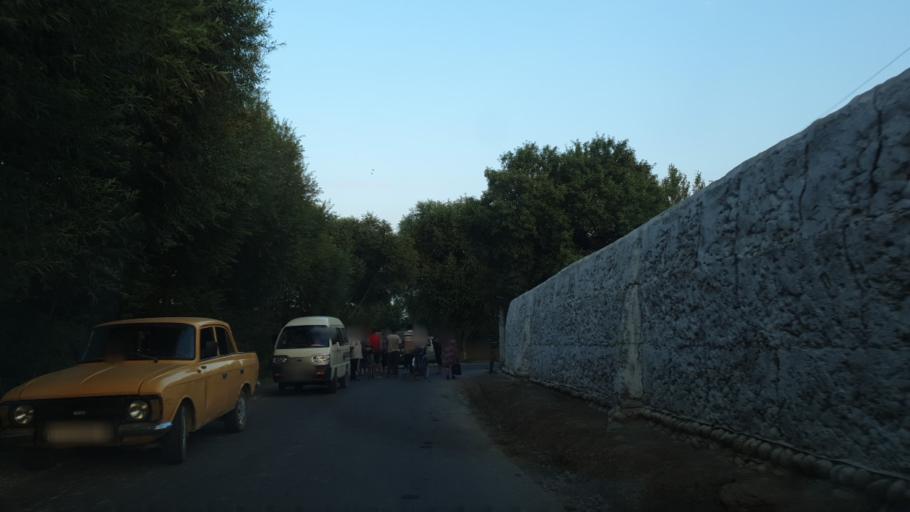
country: UZ
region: Fergana
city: Beshariq
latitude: 40.4956
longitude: 70.6219
